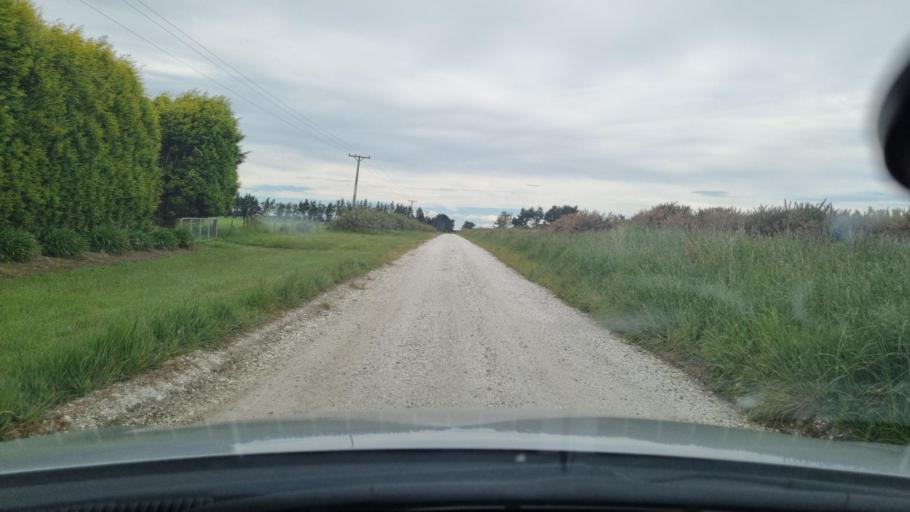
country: NZ
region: Southland
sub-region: Invercargill City
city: Invercargill
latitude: -46.4954
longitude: 168.4209
